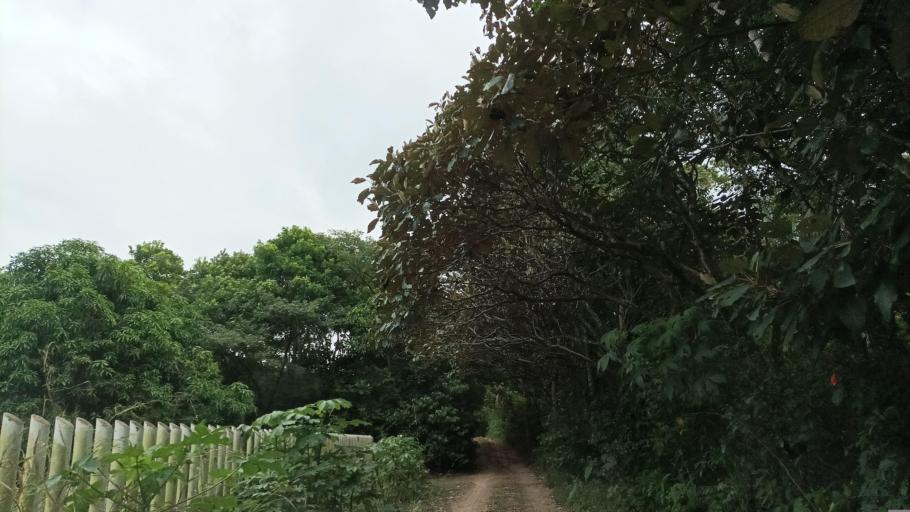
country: MX
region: Veracruz
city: Minatitlan
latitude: 18.0434
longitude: -94.5577
